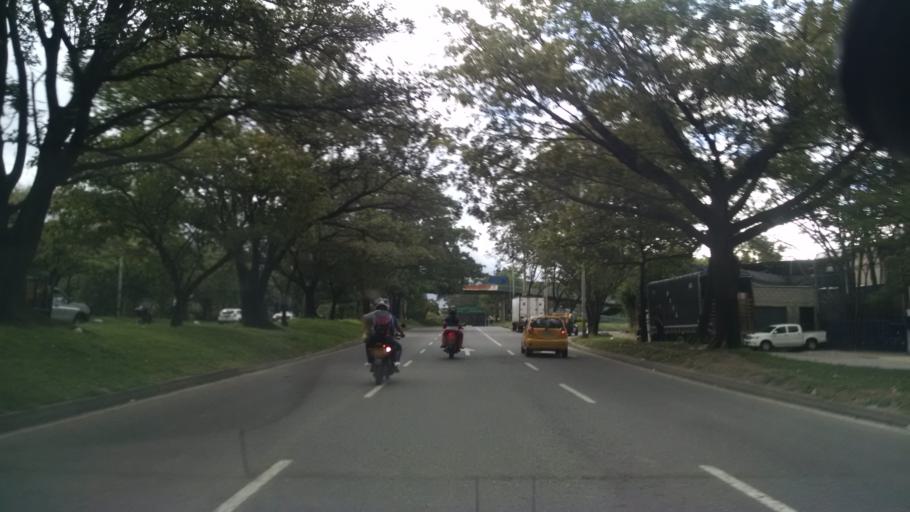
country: CO
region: Antioquia
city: Medellin
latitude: 6.2632
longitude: -75.5721
